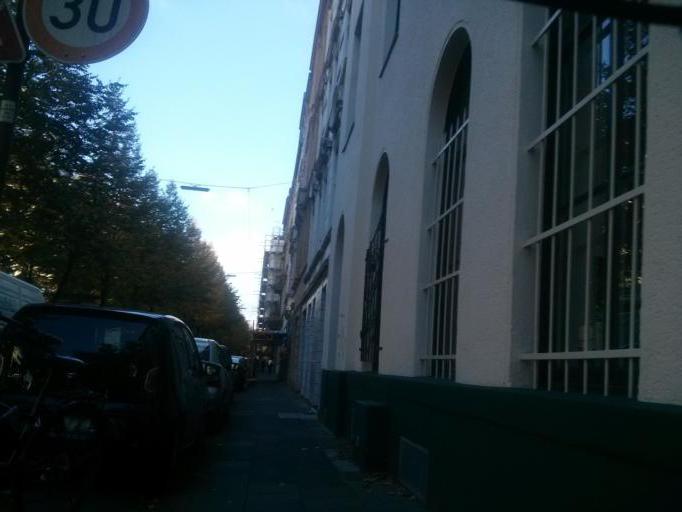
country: DE
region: North Rhine-Westphalia
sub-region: Regierungsbezirk Koln
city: Neustadt/Sued
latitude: 50.9198
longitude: 6.9538
